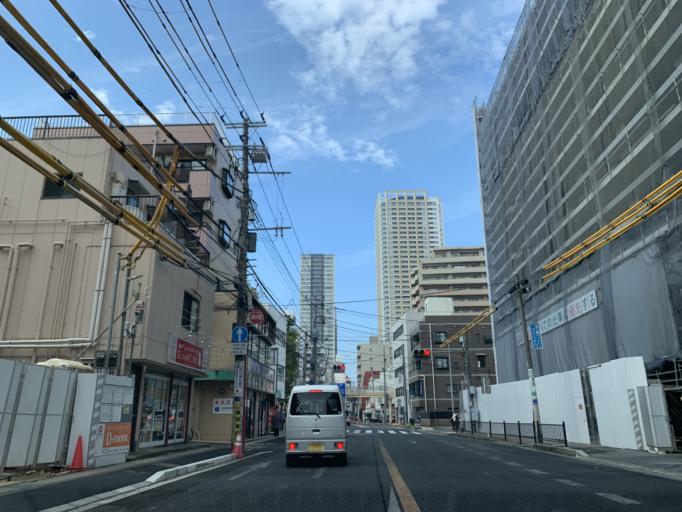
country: JP
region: Chiba
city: Funabashi
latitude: 35.7215
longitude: 139.9309
